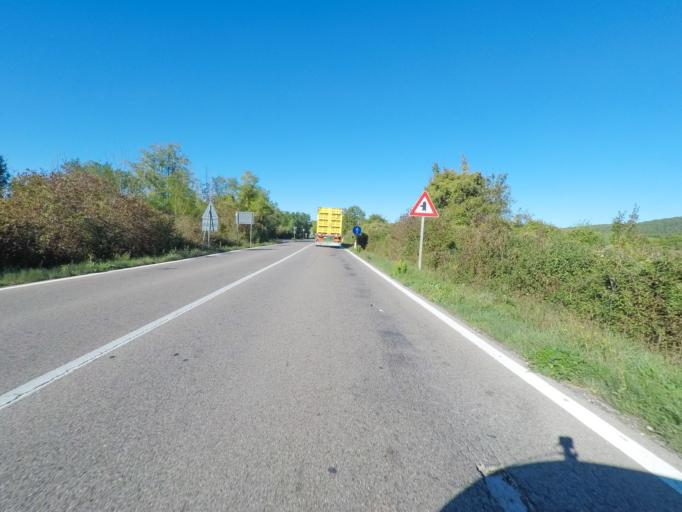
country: IT
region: Tuscany
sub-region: Provincia di Siena
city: Rosia
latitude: 43.2052
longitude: 11.2779
